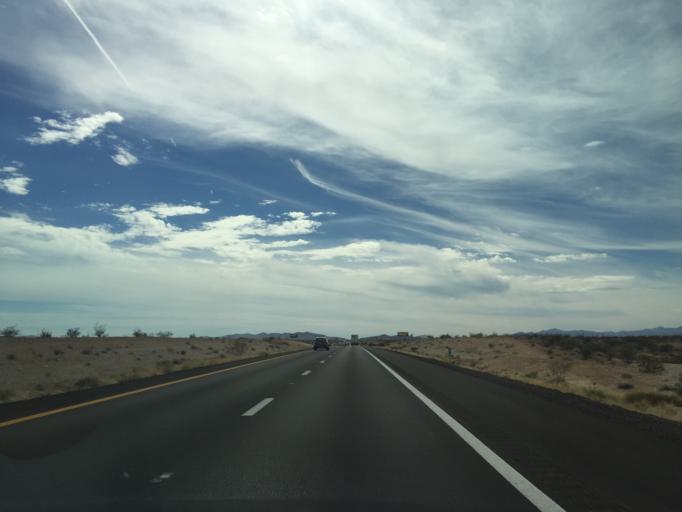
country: US
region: Nevada
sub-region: Clark County
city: Moapa Town
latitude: 36.5361
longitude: -114.7187
